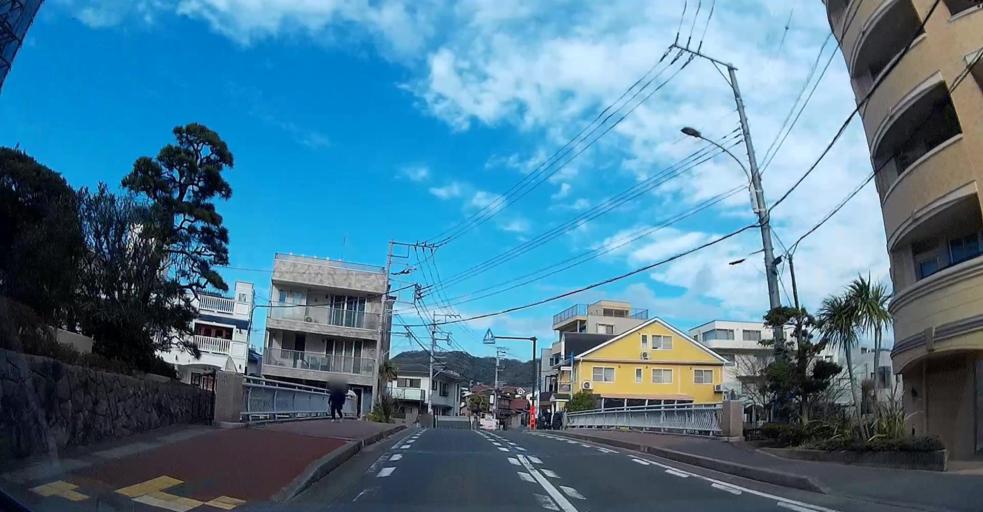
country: JP
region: Kanagawa
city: Hayama
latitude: 35.2735
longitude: 139.5720
